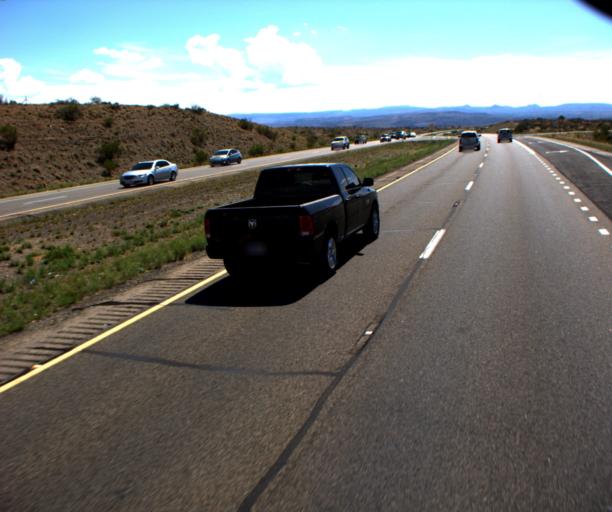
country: US
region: Arizona
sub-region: Yavapai County
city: Spring Valley
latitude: 34.3497
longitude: -112.1574
